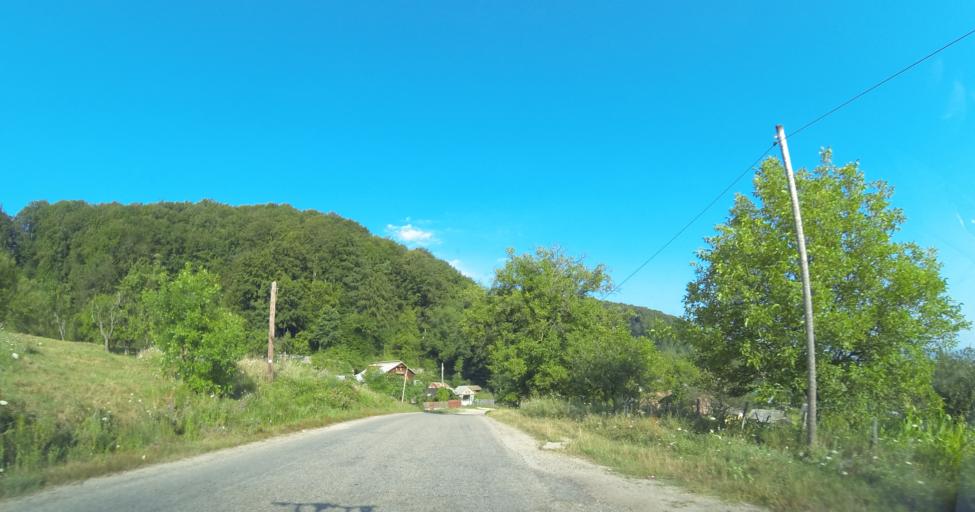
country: RO
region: Valcea
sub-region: Comuna Maldaresti
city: Maldaresti
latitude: 45.0965
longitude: 24.0118
